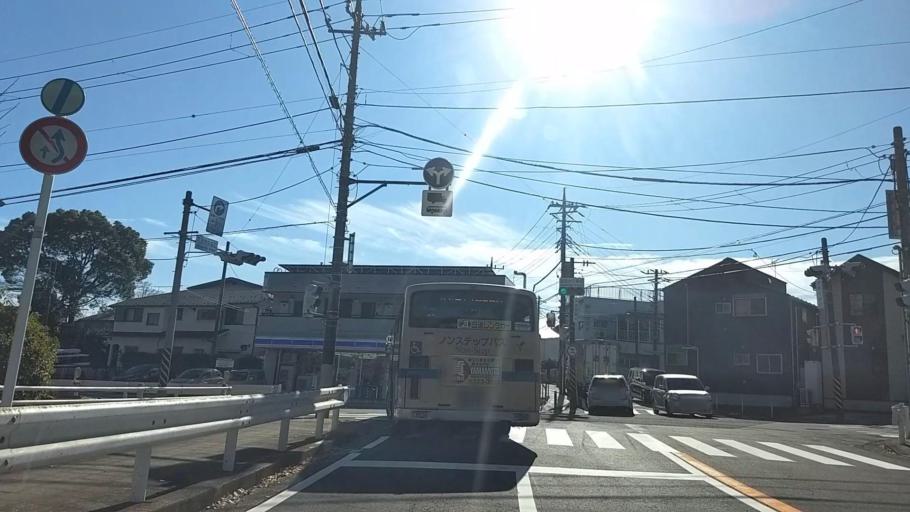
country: JP
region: Kanagawa
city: Yokohama
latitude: 35.4521
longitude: 139.5815
